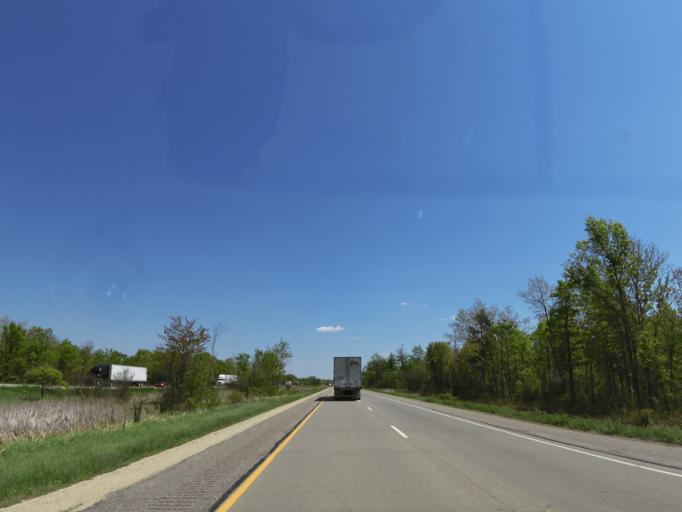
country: US
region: Wisconsin
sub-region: Juneau County
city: New Lisbon
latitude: 43.9081
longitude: -90.2234
